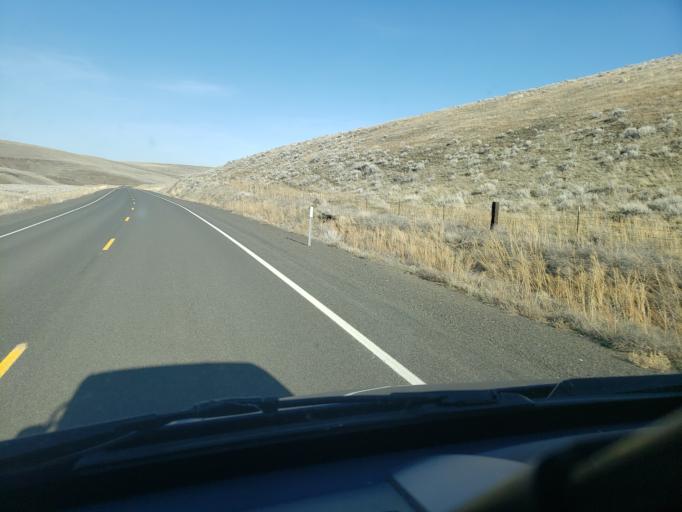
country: US
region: Oregon
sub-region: Umatilla County
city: Pilot Rock
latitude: 45.4615
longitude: -118.9303
